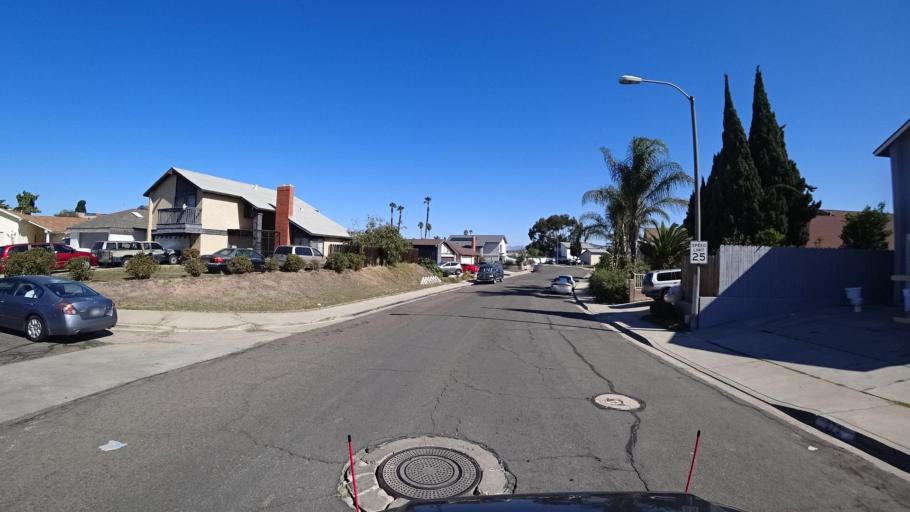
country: US
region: California
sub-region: San Diego County
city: La Presa
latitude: 32.6998
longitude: -117.0273
